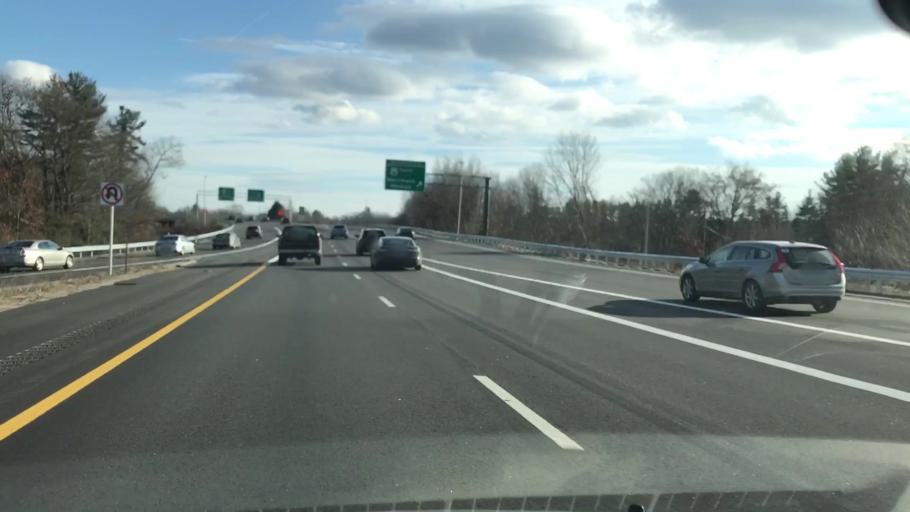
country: US
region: New Hampshire
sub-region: Hillsborough County
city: Bedford
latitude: 42.9494
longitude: -71.4751
